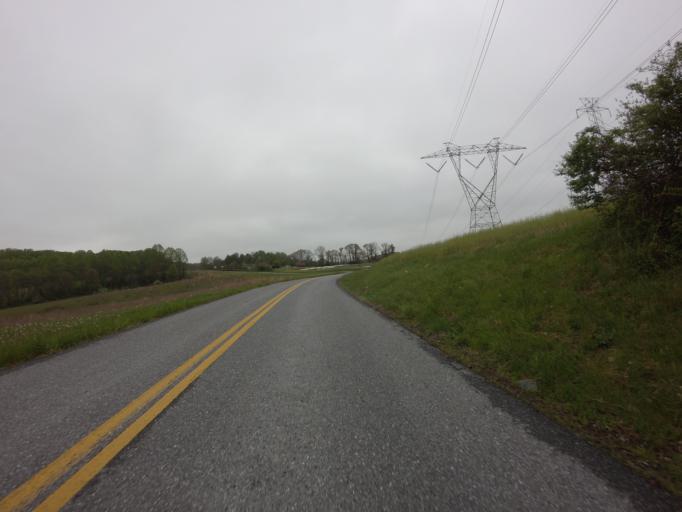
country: US
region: Maryland
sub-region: Carroll County
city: Hampstead
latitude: 39.5702
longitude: -76.7527
